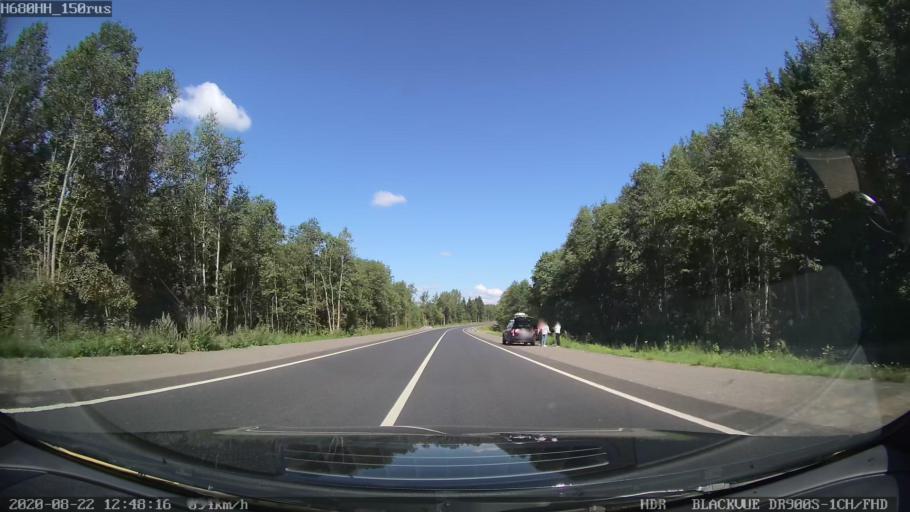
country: RU
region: Tverskaya
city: Rameshki
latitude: 57.4375
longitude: 36.1827
